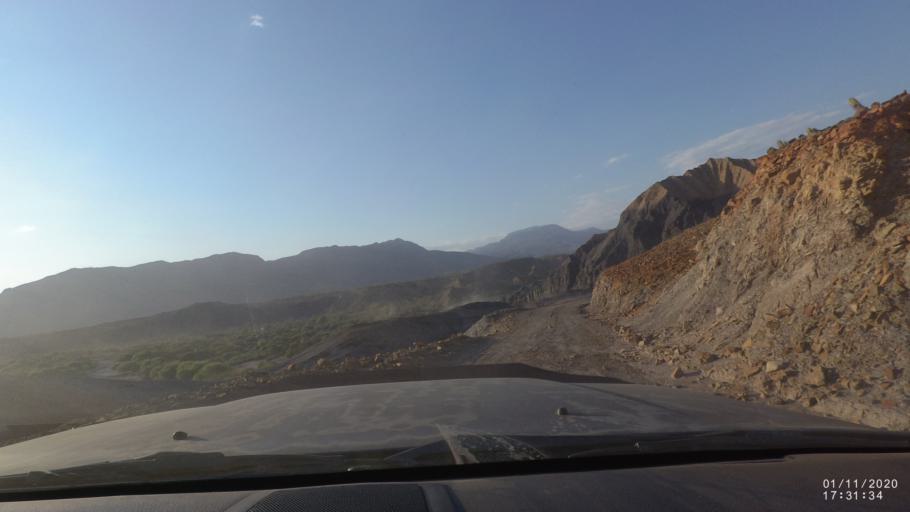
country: BO
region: Chuquisaca
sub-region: Provincia Zudanez
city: Mojocoya
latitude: -18.6757
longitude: -64.5227
